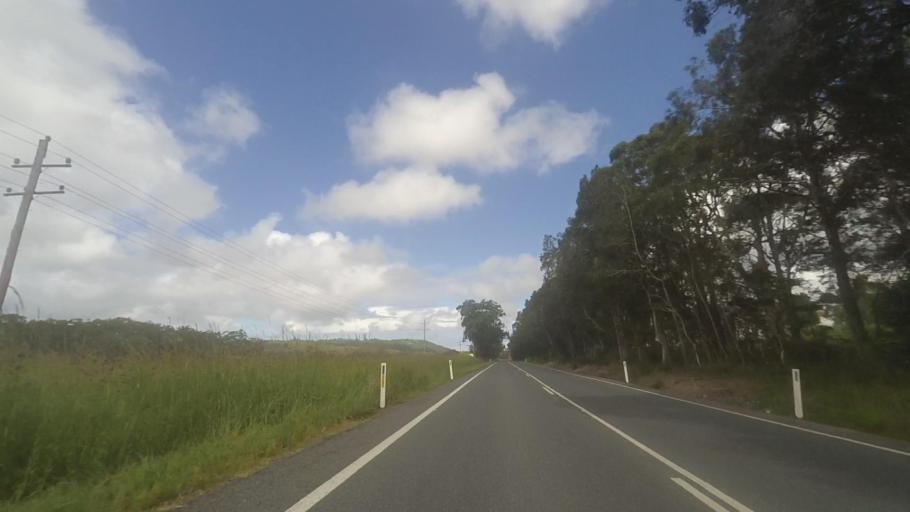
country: AU
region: New South Wales
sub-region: Great Lakes
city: Bulahdelah
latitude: -32.3855
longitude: 152.4059
